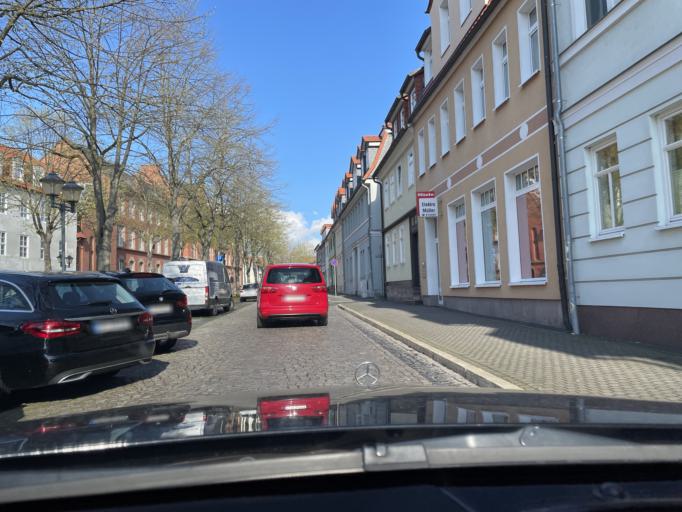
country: DE
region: Thuringia
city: Heilbad Heiligenstadt
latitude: 51.3794
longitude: 10.1357
